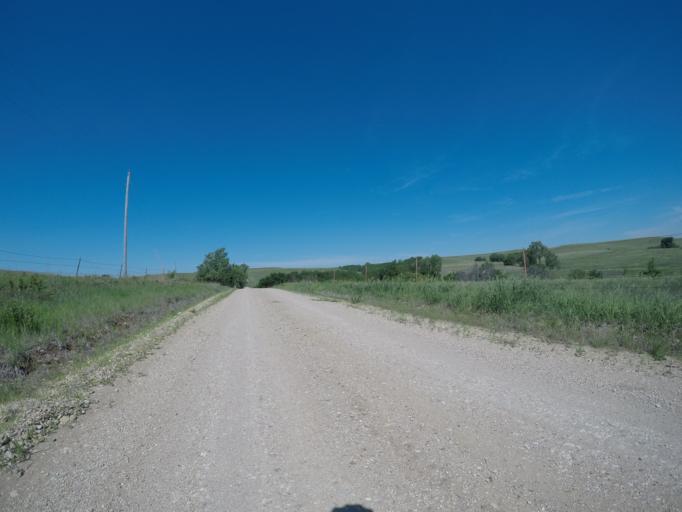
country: US
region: Kansas
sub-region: Wabaunsee County
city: Alma
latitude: 39.0152
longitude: -96.1581
